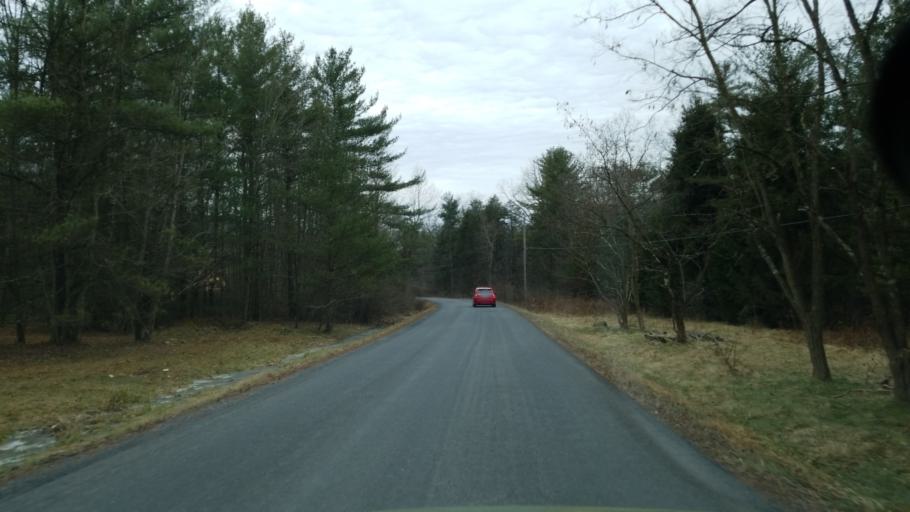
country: US
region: Pennsylvania
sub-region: Centre County
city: Centre Hall
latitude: 40.7714
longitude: -77.6816
